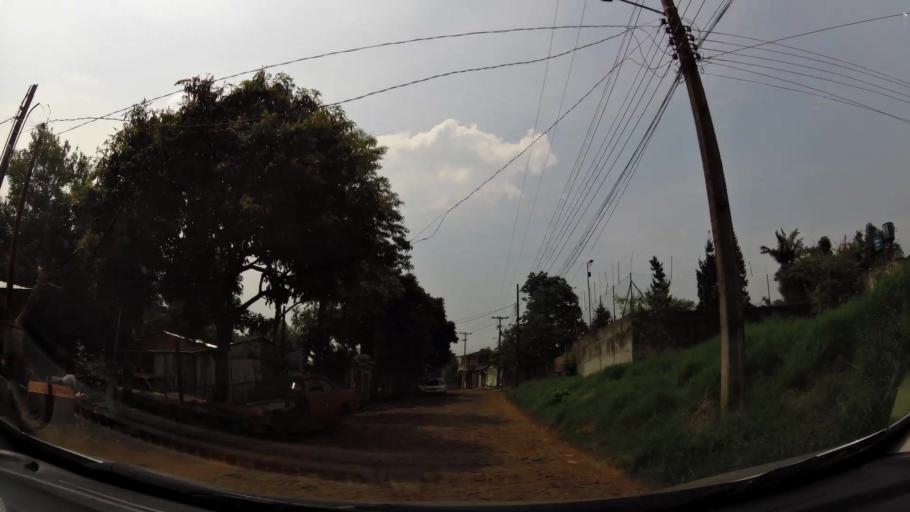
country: PY
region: Alto Parana
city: Presidente Franco
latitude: -25.5452
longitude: -54.6244
